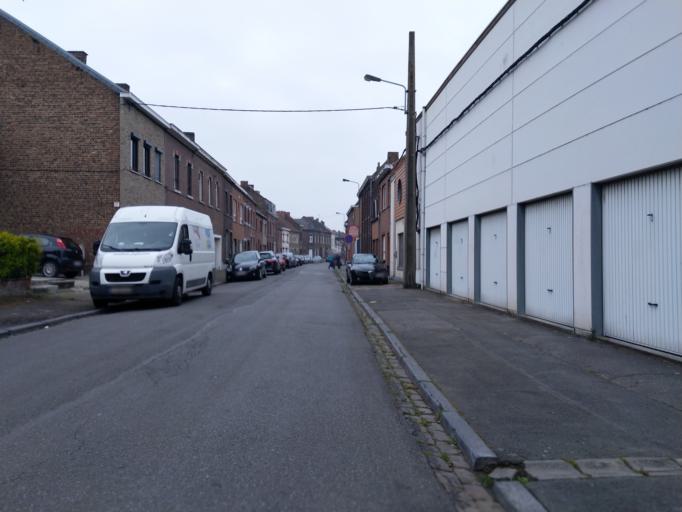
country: BE
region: Wallonia
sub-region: Province du Hainaut
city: Quaregnon
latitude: 50.4517
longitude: 3.8825
